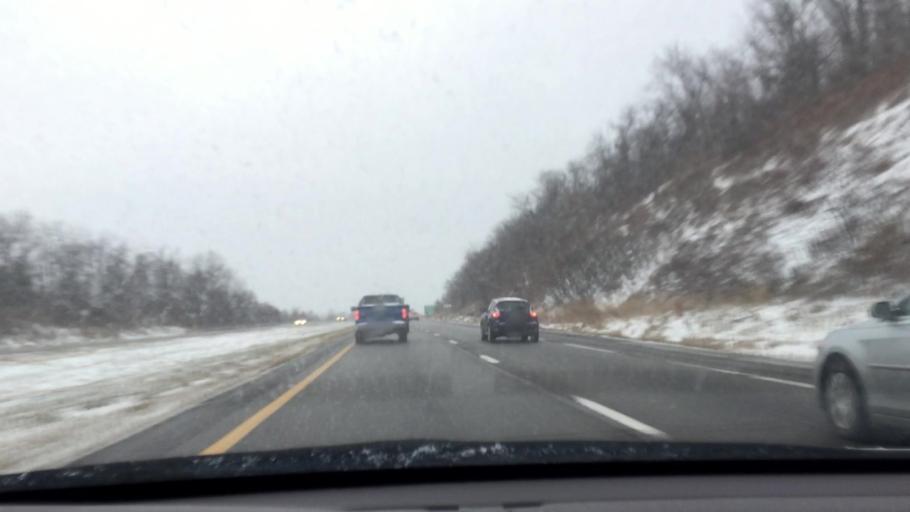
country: US
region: Pennsylvania
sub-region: Washington County
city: Canonsburg
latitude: 40.2846
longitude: -80.1656
